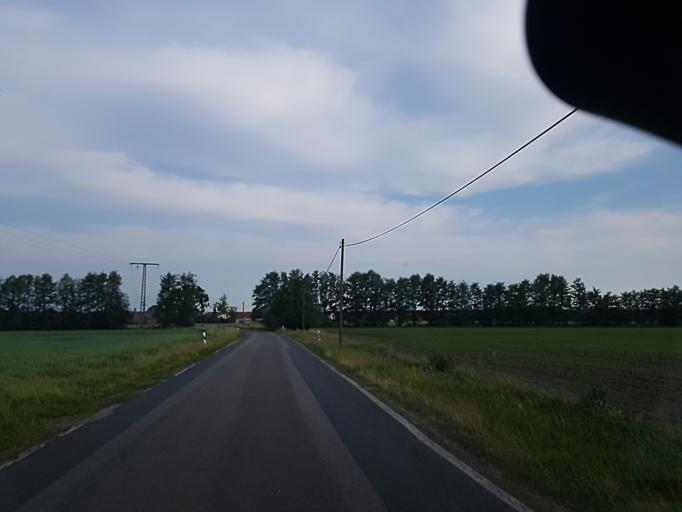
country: DE
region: Saxony-Anhalt
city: Jessen
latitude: 51.8308
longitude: 12.9458
